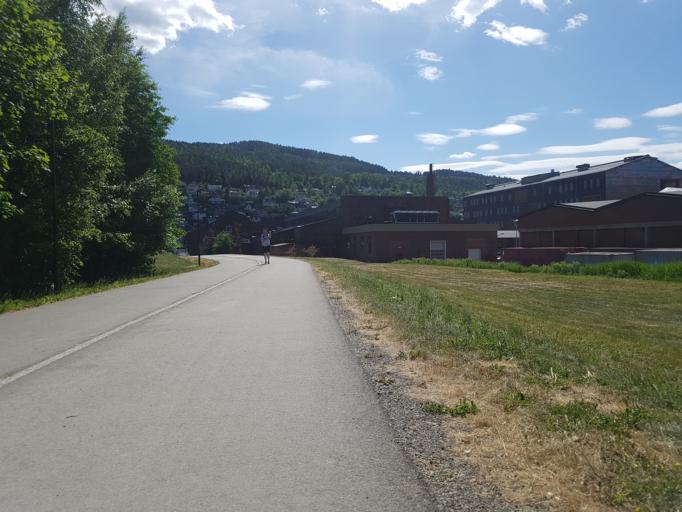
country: NO
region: Buskerud
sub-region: Drammen
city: Drammen
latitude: 59.7412
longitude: 10.1836
